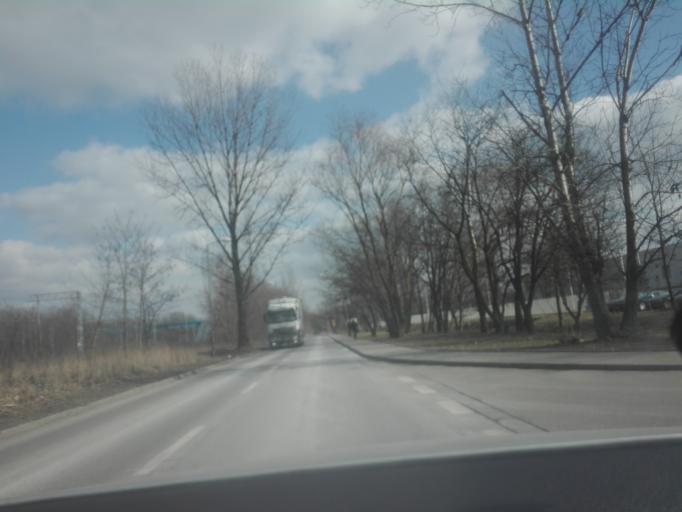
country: PL
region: Silesian Voivodeship
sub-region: Katowice
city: Katowice
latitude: 50.2621
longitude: 18.9946
